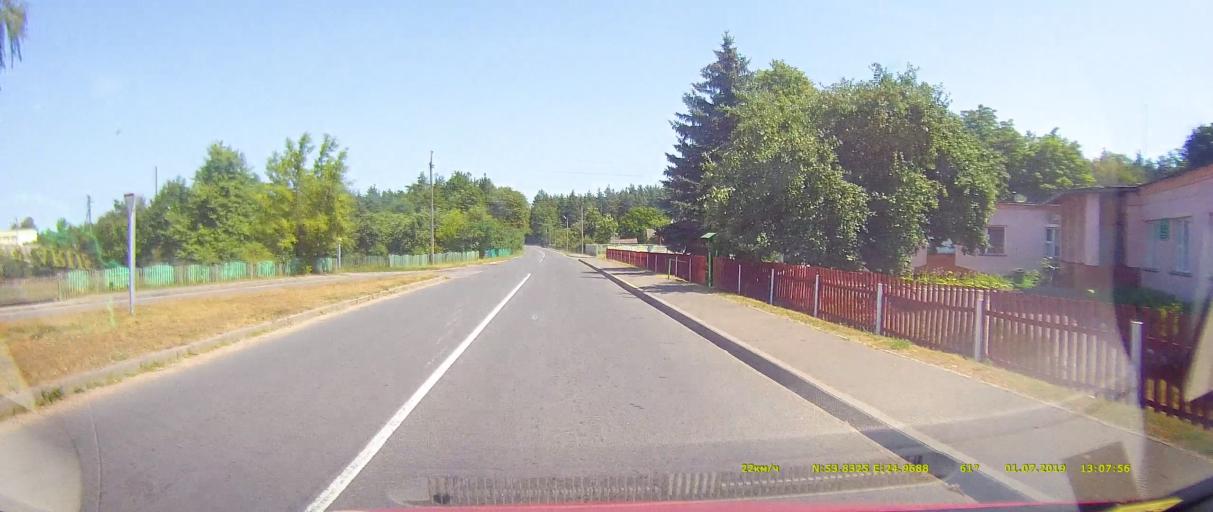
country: BY
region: Grodnenskaya
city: Shchuchin
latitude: 53.8324
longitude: 24.9687
